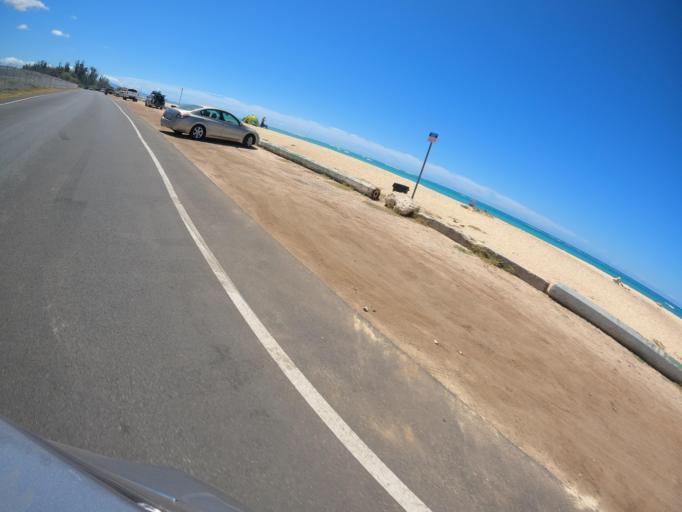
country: US
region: Hawaii
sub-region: Honolulu County
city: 'Ewa Villages
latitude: 21.3000
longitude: -158.0629
